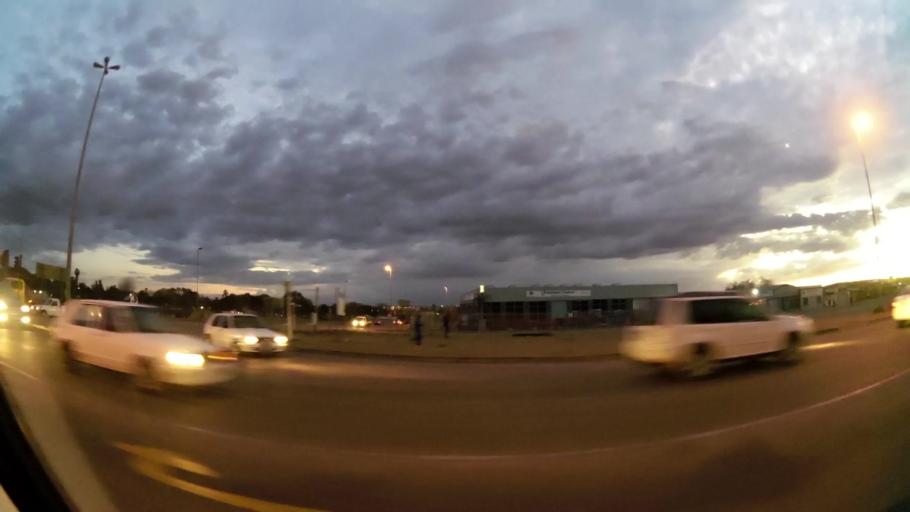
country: ZA
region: Limpopo
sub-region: Capricorn District Municipality
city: Polokwane
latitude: -23.8760
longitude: 29.4410
